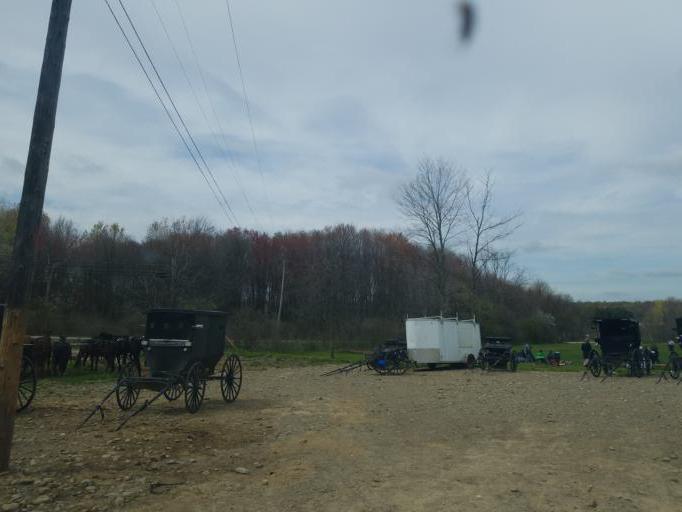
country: US
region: Pennsylvania
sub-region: Mercer County
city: Stoneboro
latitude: 41.4178
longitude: -80.0744
